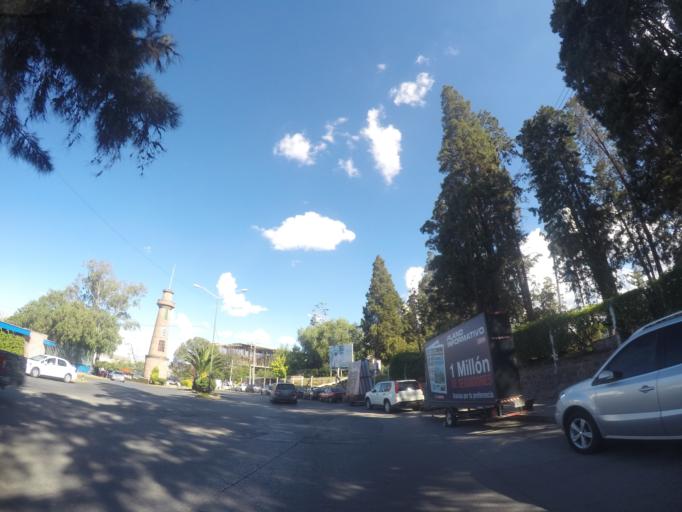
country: MX
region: San Luis Potosi
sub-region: San Luis Potosi
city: San Luis Potosi
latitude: 22.1483
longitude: -101.0195
